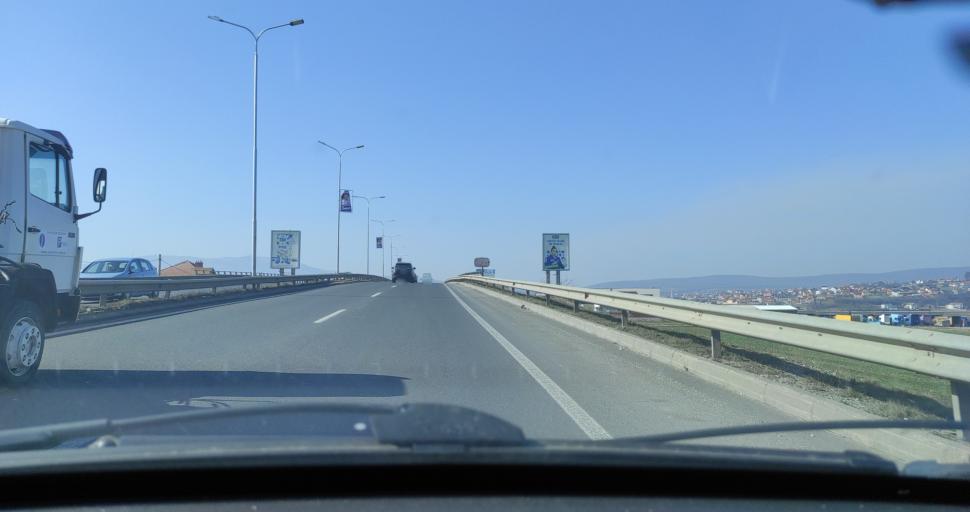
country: XK
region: Pristina
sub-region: Komuna e Gracanices
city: Glanica
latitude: 42.6046
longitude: 21.0419
